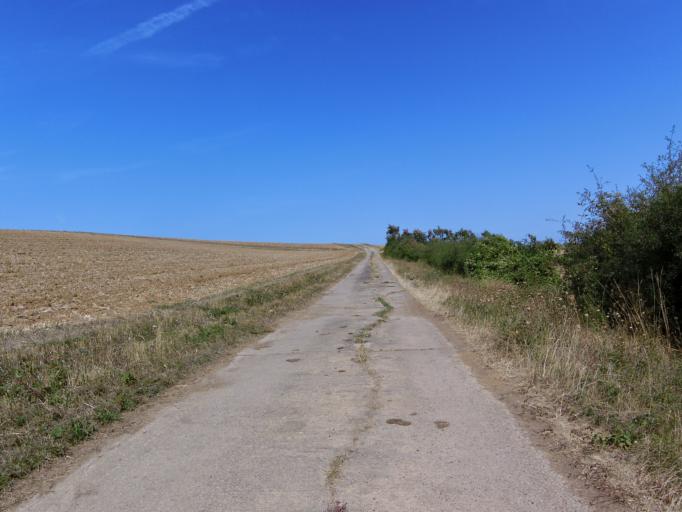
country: DE
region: Bavaria
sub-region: Regierungsbezirk Unterfranken
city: Theilheim
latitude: 49.7658
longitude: 10.0293
